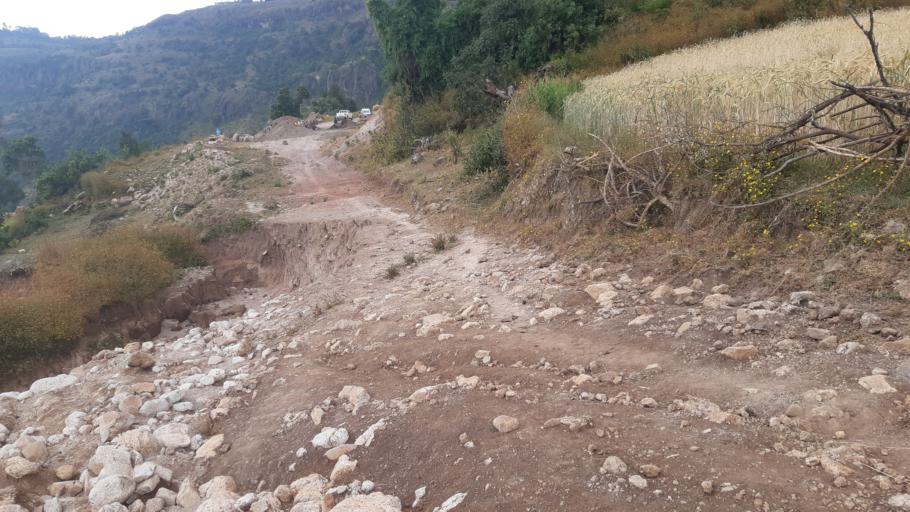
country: ET
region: Amhara
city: Dabat
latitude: 13.3419
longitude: 37.4064
